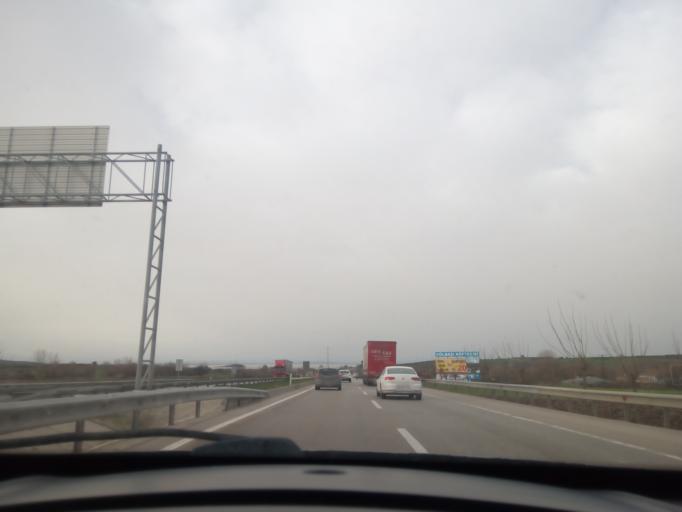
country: TR
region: Bursa
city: Mahmudiye
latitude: 40.2142
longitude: 28.6208
